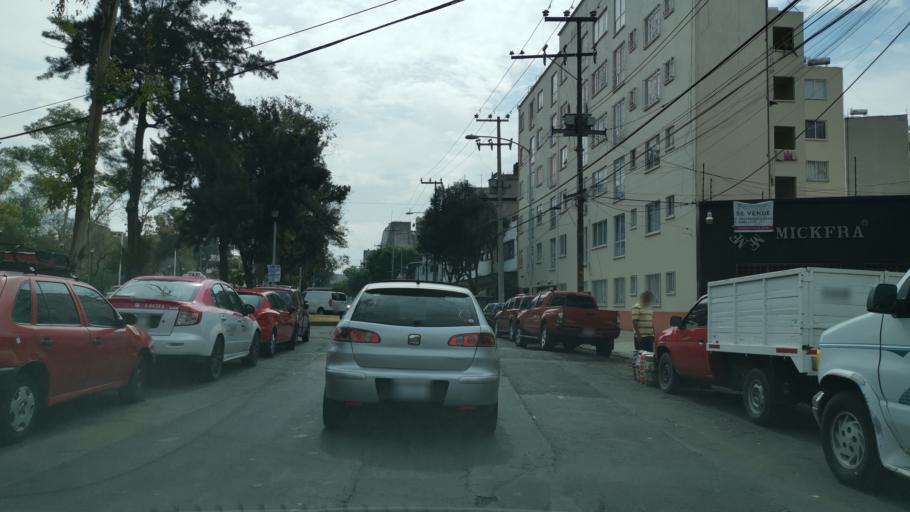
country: MX
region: Mexico City
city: Mexico City
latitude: 19.4227
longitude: -99.1283
